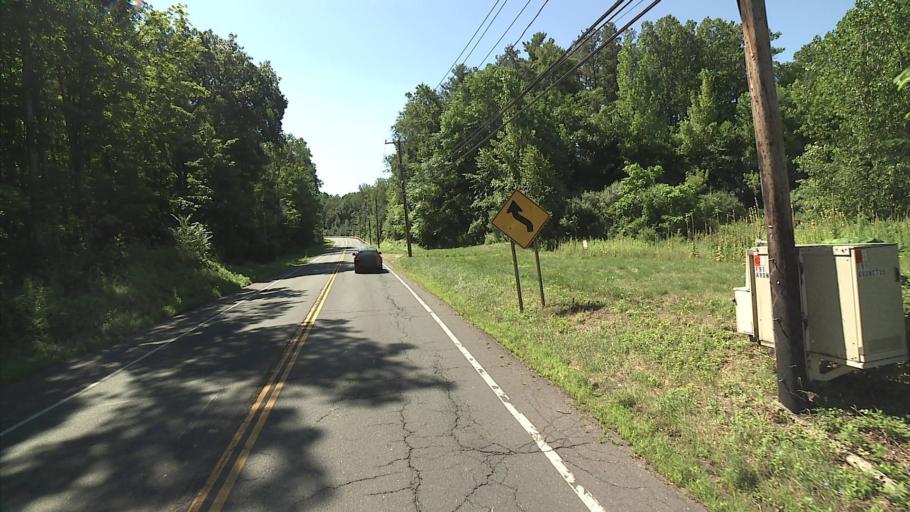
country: US
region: Connecticut
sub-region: Hartford County
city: Weatogue
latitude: 41.7996
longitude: -72.8189
